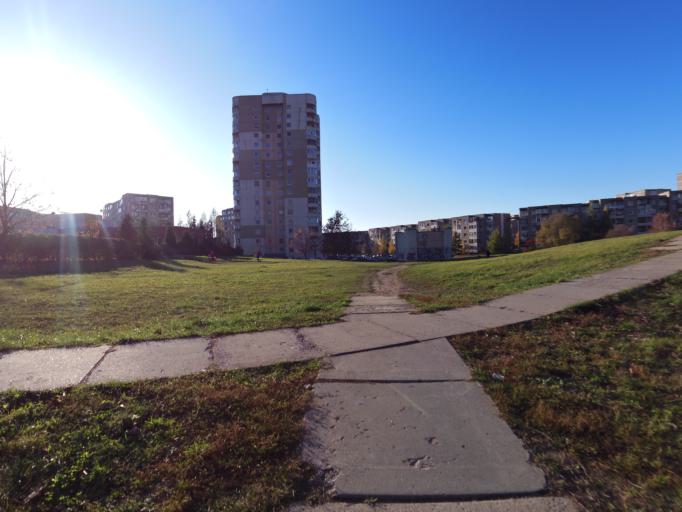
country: LT
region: Vilnius County
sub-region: Vilnius
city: Fabijoniskes
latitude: 54.7342
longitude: 25.2409
